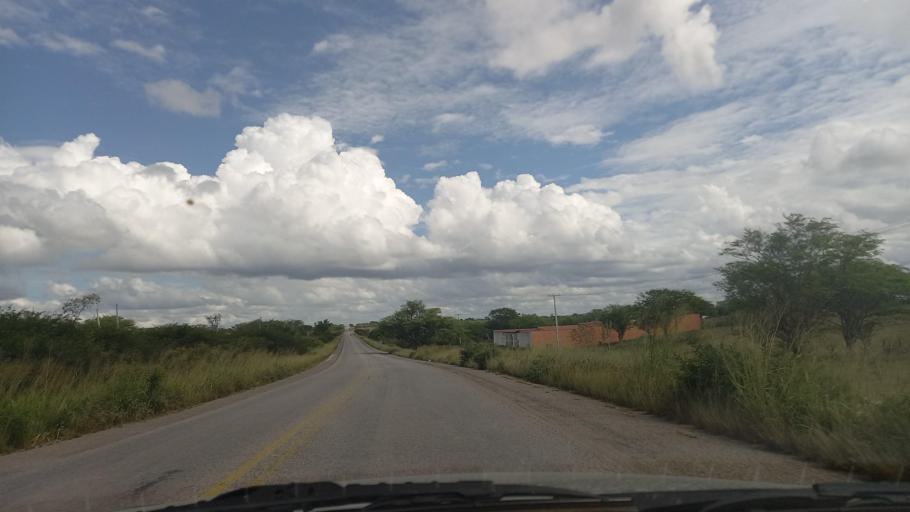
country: BR
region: Pernambuco
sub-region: Cachoeirinha
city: Cachoeirinha
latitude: -8.4479
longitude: -36.2099
